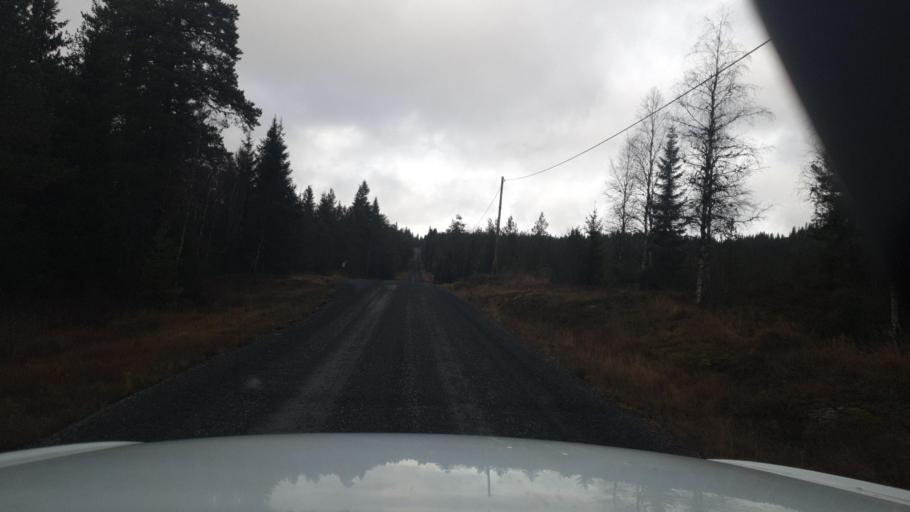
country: SE
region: Vaermland
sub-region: Torsby Kommun
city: Torsby
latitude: 60.1645
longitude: 12.6163
